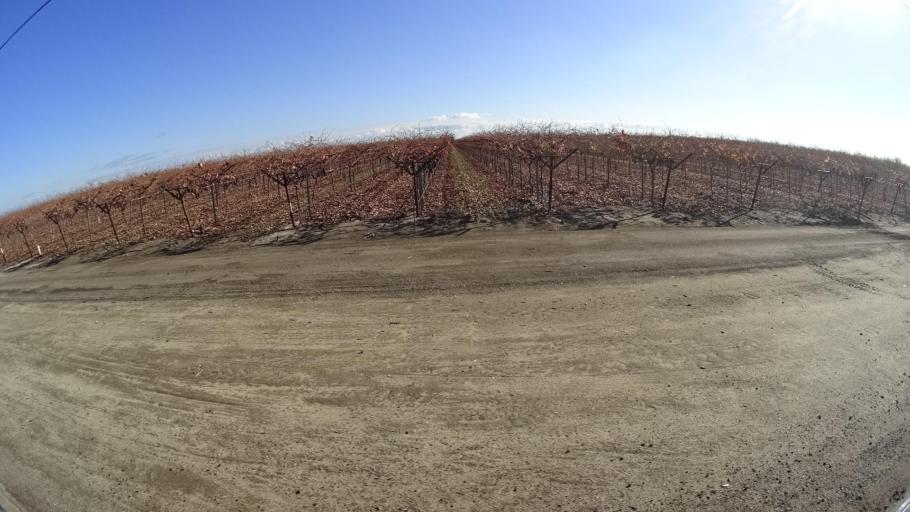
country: US
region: California
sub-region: Kern County
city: McFarland
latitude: 35.7111
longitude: -119.2764
